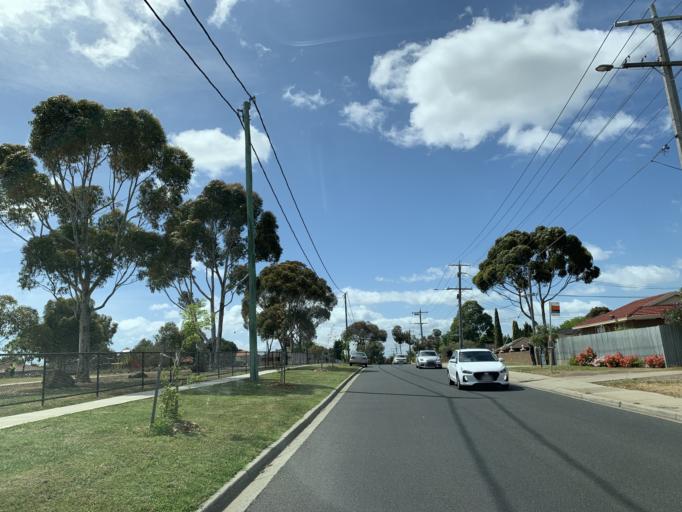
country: AU
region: Victoria
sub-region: Brimbank
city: Kealba
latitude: -37.7385
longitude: 144.8151
